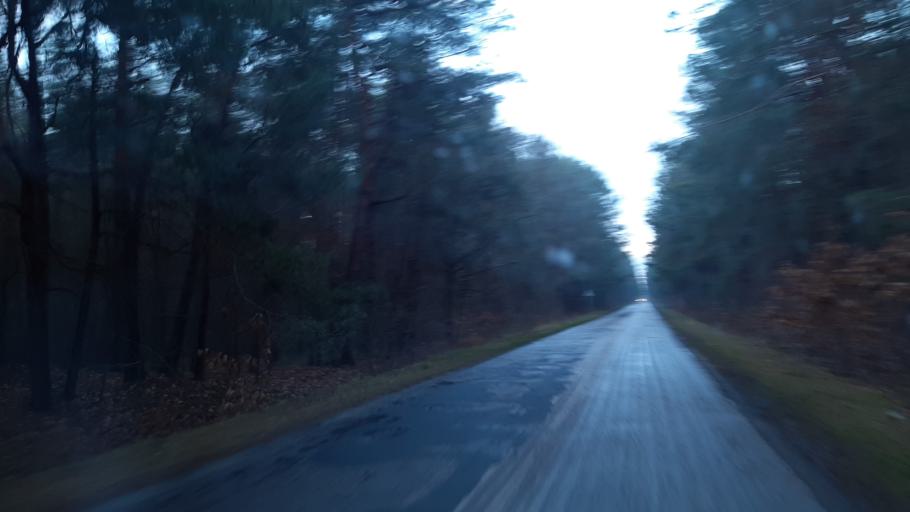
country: PL
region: Lublin Voivodeship
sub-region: Powiat lubartowski
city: Kamionka
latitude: 51.4803
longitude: 22.4709
